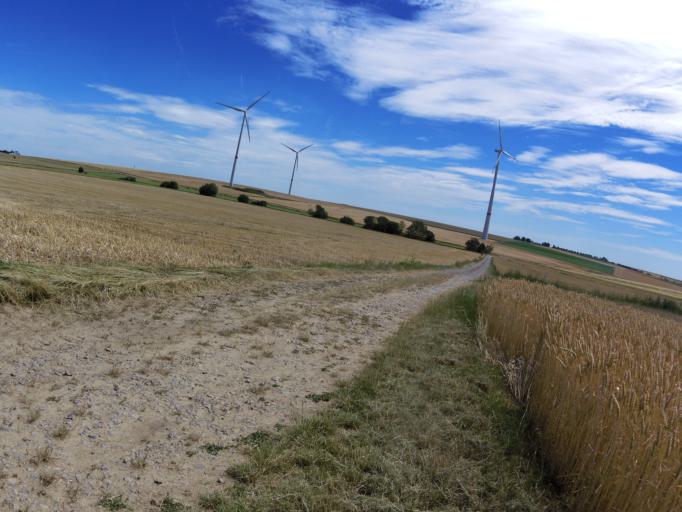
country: DE
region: Bavaria
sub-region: Regierungsbezirk Unterfranken
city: Geroldshausen
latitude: 49.7014
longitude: 9.8815
